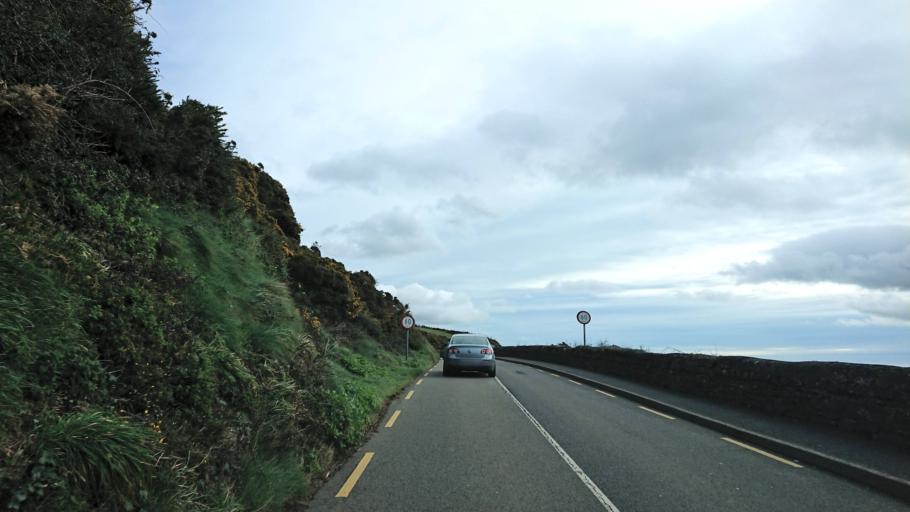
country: IE
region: Munster
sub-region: Waterford
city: Dunmore East
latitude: 52.2440
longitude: -6.9667
